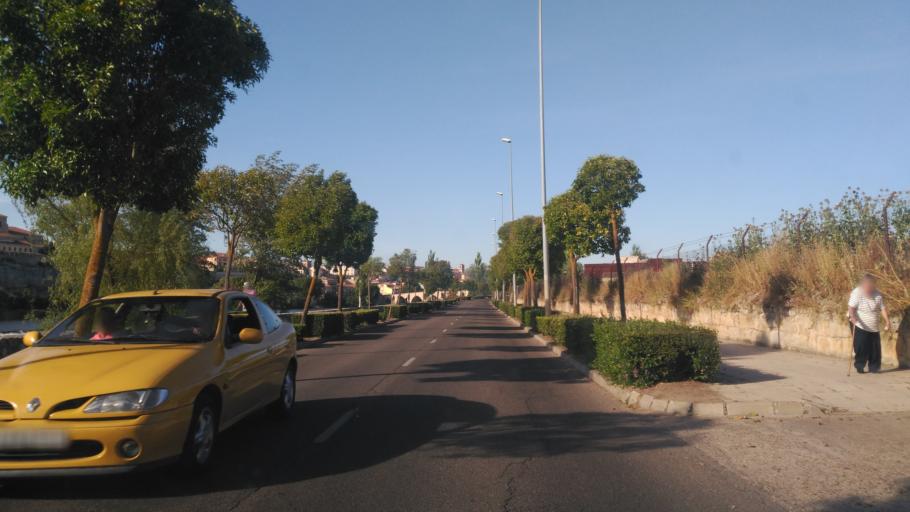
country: ES
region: Castille and Leon
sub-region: Provincia de Zamora
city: Zamora
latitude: 41.4960
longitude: -5.7521
